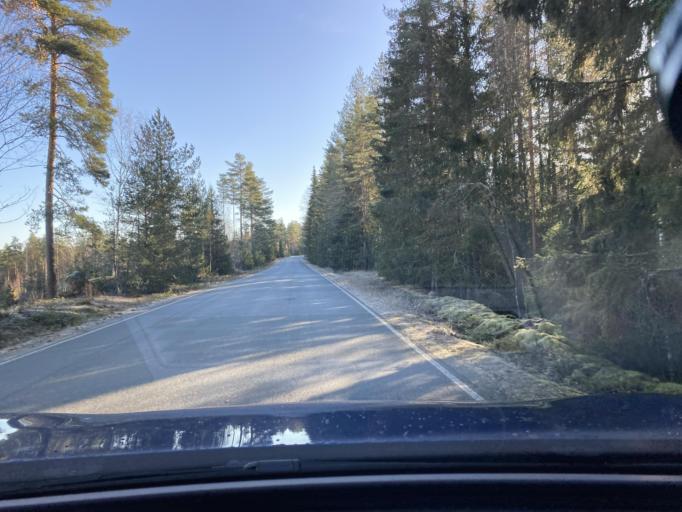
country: FI
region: Pirkanmaa
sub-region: Etelae-Pirkanmaa
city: Kylmaekoski
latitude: 61.0602
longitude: 23.6728
